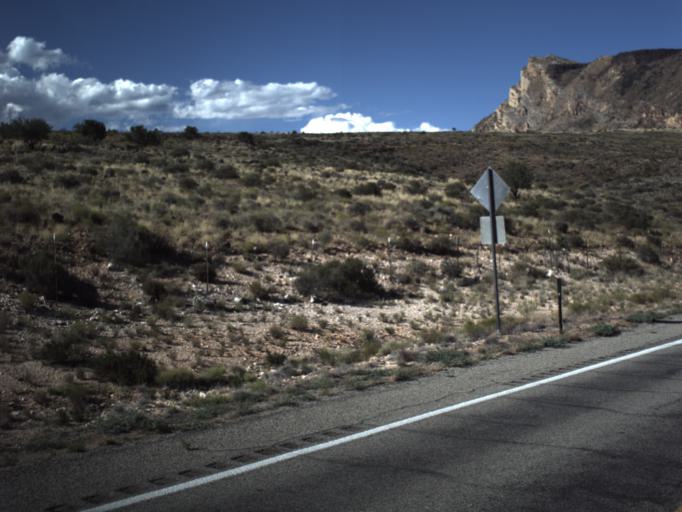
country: US
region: Utah
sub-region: Washington County
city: Toquerville
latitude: 37.2596
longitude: -113.2910
